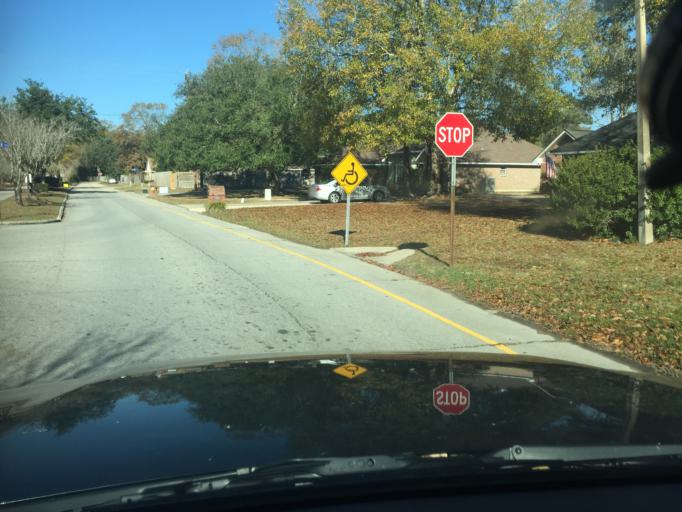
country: US
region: Louisiana
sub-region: Saint Tammany Parish
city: Slidell
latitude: 30.2992
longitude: -89.7241
